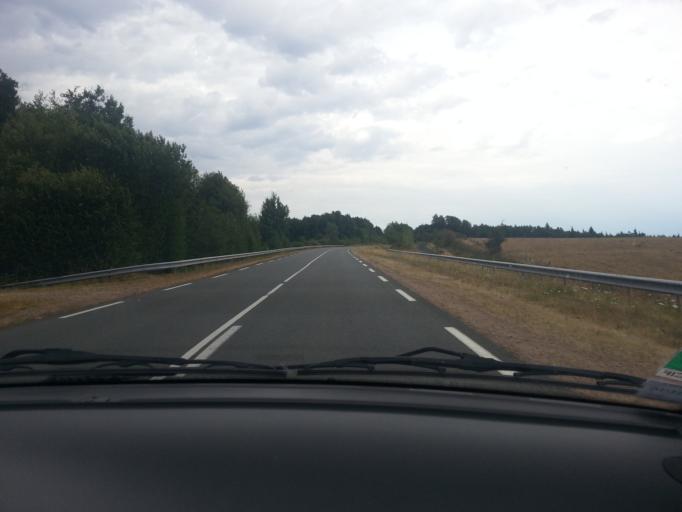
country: FR
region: Auvergne
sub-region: Departement de l'Allier
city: Lapalisse
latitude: 46.2295
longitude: 3.6873
